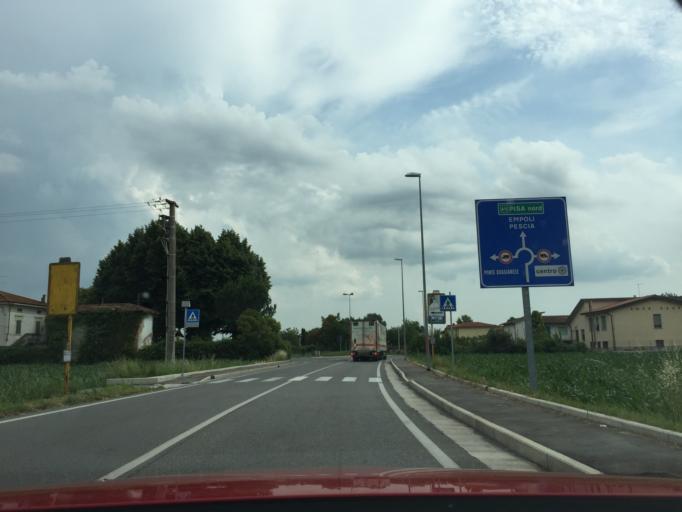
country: IT
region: Tuscany
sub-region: Provincia di Pistoia
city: Chiesina Uzzanese
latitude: 43.8402
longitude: 10.7266
